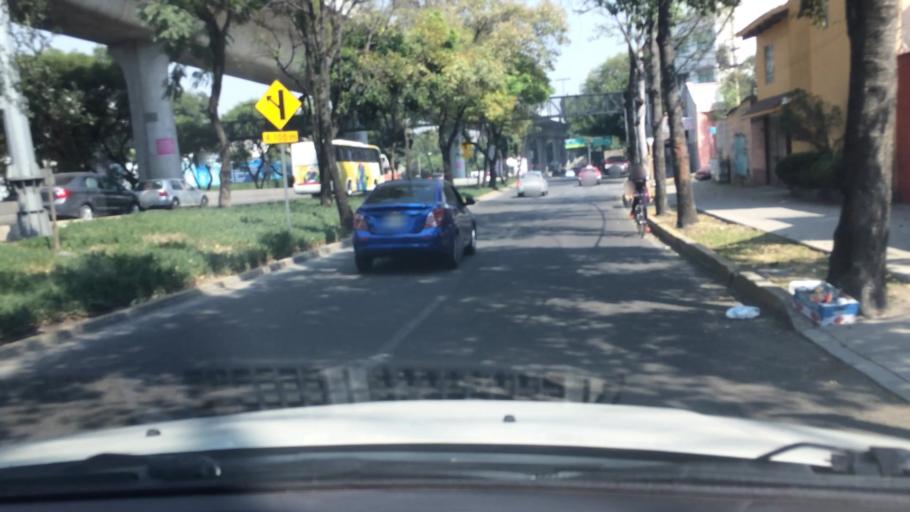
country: MX
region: Mexico City
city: Tlalpan
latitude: 19.2841
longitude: -99.1604
